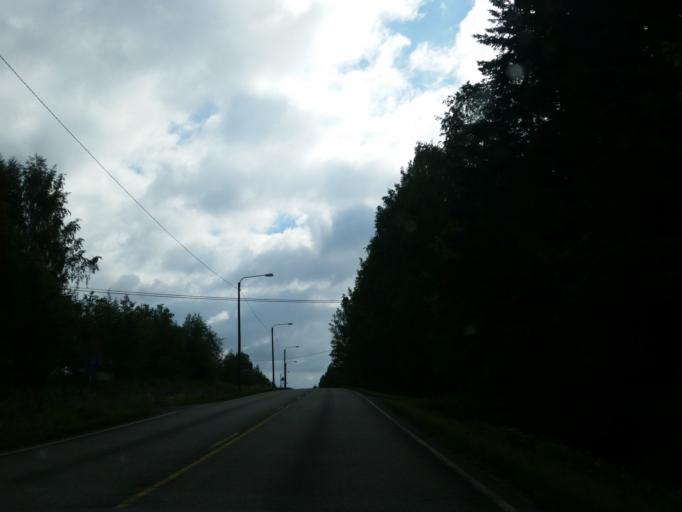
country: FI
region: Northern Savo
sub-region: Sisae-Savo
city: Suonenjoki
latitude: 62.8426
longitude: 27.3351
